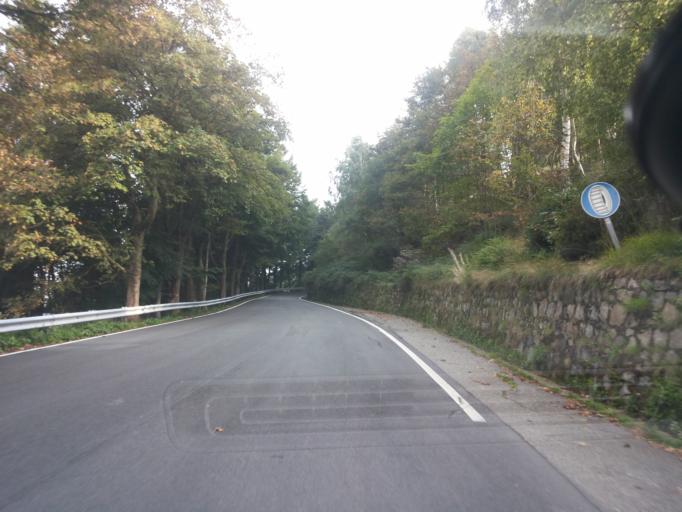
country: IT
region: Piedmont
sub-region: Provincia di Biella
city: Portula
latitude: 45.6814
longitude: 8.1428
